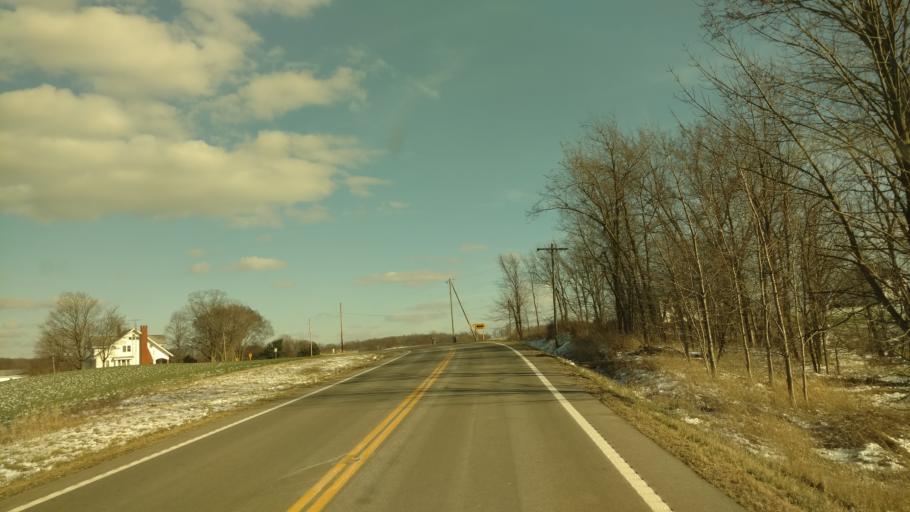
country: US
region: Ohio
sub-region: Ashland County
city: Loudonville
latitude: 40.7411
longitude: -82.2457
